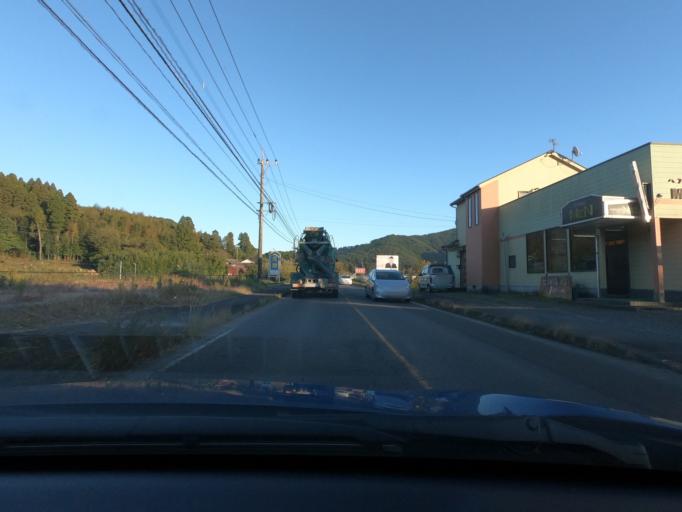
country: JP
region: Kagoshima
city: Satsumasendai
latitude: 31.8059
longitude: 130.3474
